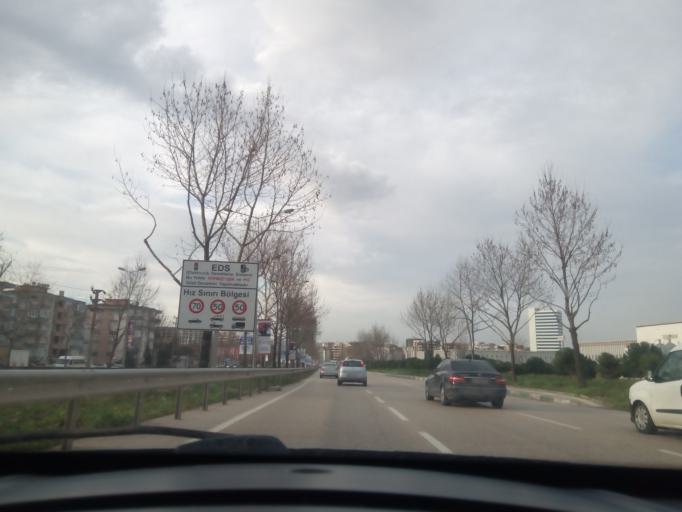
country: TR
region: Bursa
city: Niluefer
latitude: 40.2239
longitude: 28.9576
